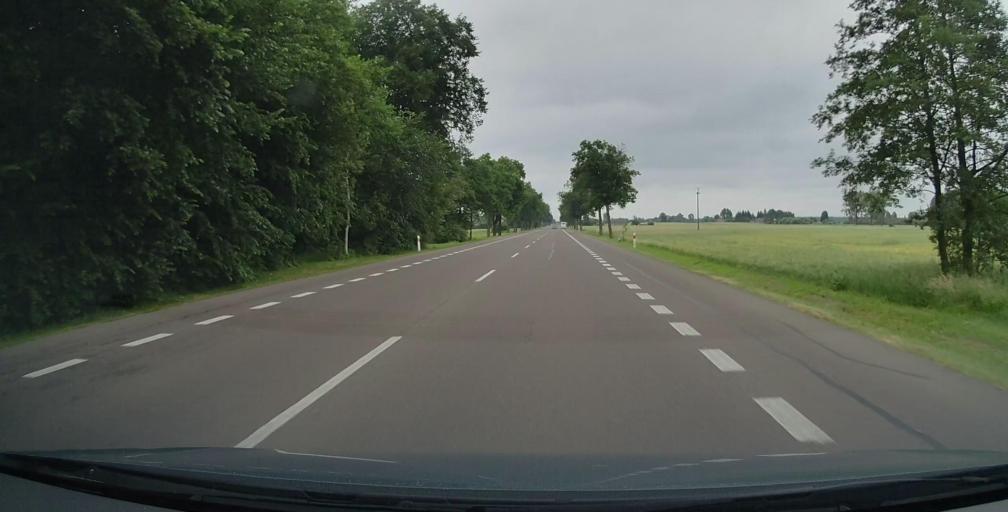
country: PL
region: Lublin Voivodeship
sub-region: Powiat bialski
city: Rzeczyca
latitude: 52.0411
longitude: 22.6877
